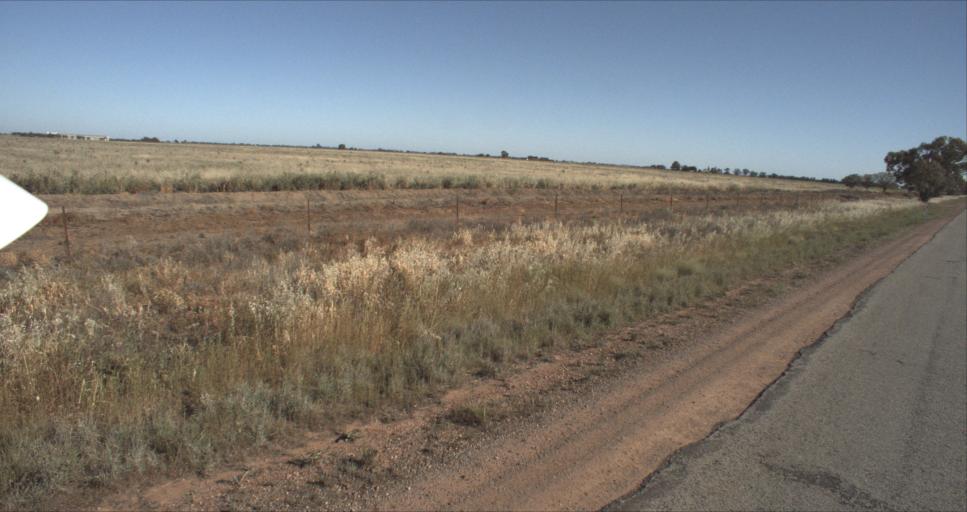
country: AU
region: New South Wales
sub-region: Leeton
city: Leeton
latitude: -34.5623
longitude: 146.3125
